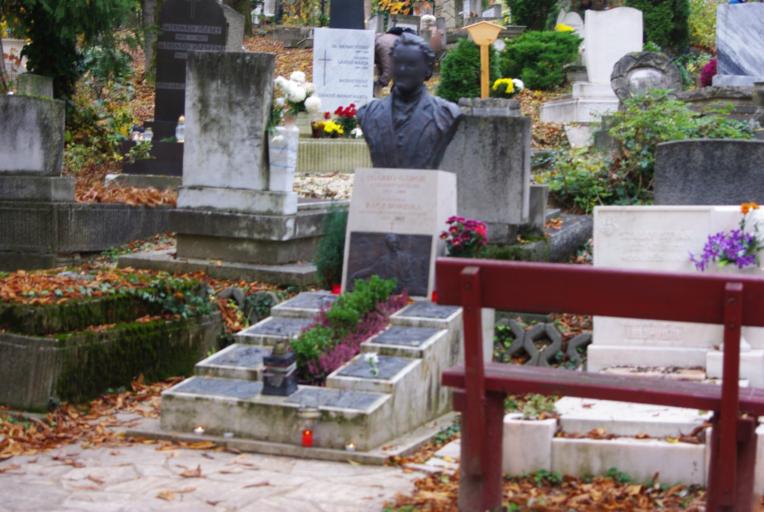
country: HU
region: Budapest
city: Budapest XII. keruelet
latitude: 47.4855
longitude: 19.0004
